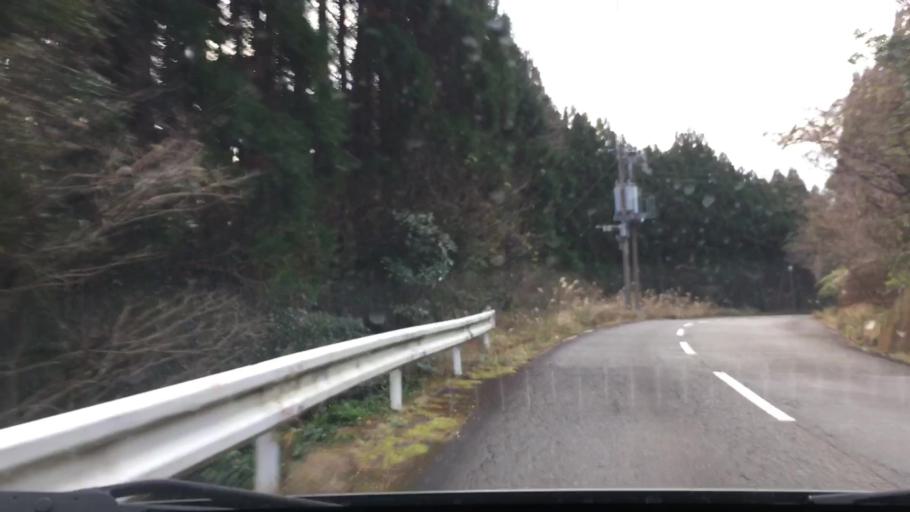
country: JP
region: Miyazaki
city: Nichinan
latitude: 31.6616
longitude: 131.3210
